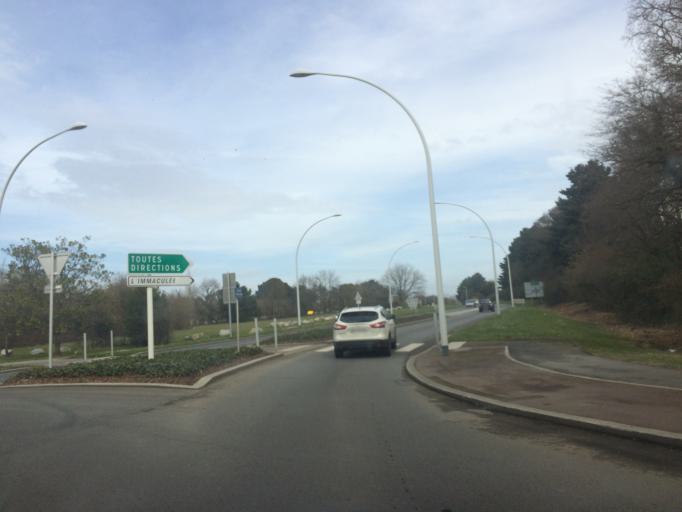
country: FR
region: Pays de la Loire
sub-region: Departement de la Loire-Atlantique
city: Saint-Nazaire
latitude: 47.2680
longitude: -2.2529
